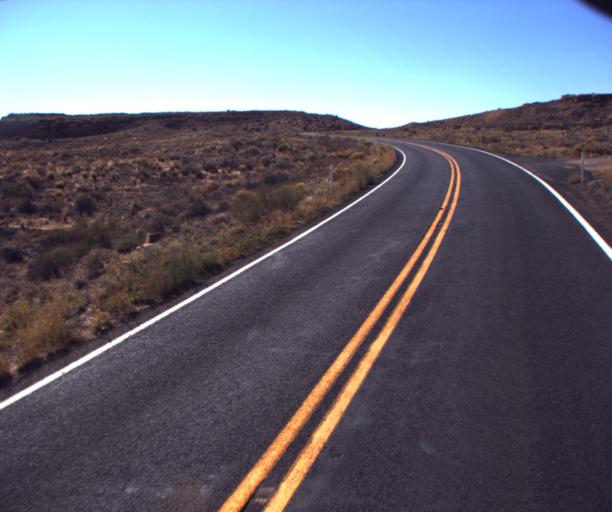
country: US
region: Arizona
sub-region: Navajo County
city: First Mesa
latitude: 35.8829
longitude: -110.6220
